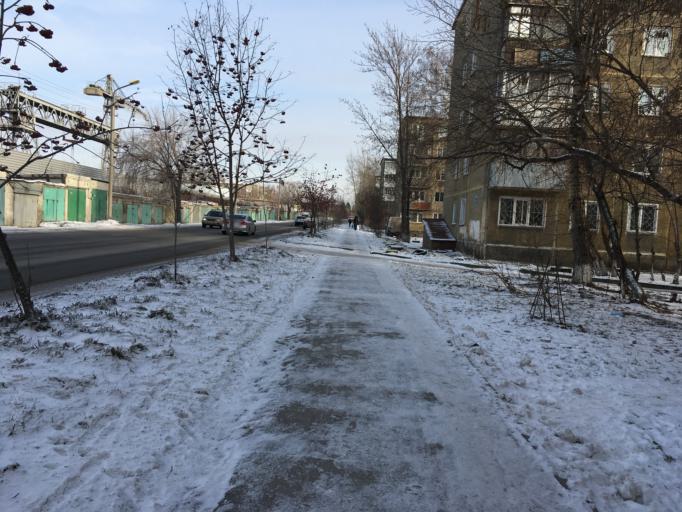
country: RU
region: Novosibirsk
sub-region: Novosibirskiy Rayon
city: Novosibirsk
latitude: 55.0570
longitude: 82.9709
